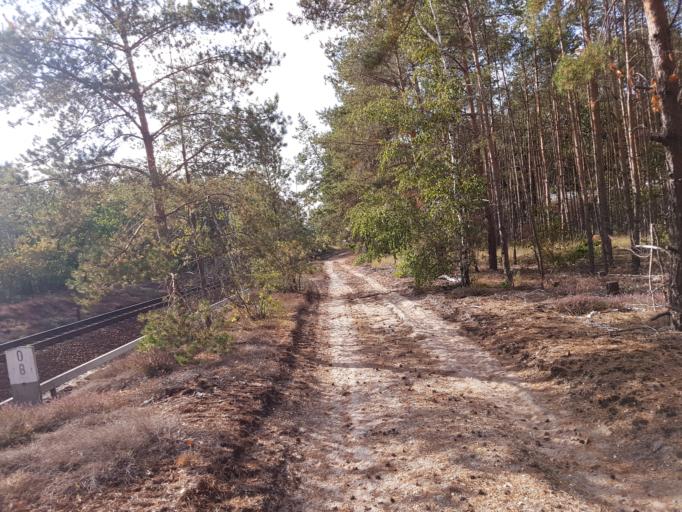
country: DE
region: Brandenburg
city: Doberlug-Kirchhain
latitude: 51.6293
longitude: 13.5937
